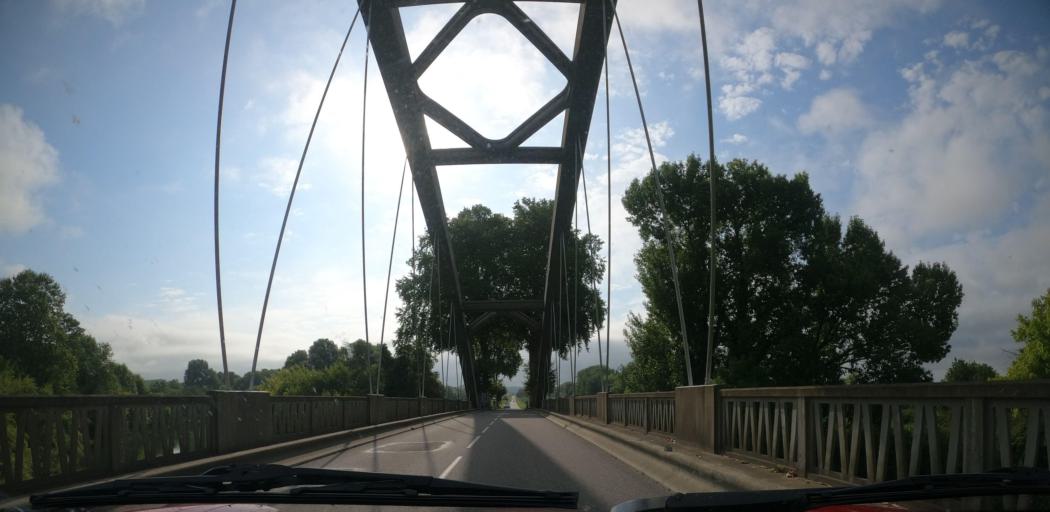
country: FR
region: Aquitaine
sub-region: Departement des Landes
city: Peyrehorade
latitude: 43.5411
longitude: -1.0882
